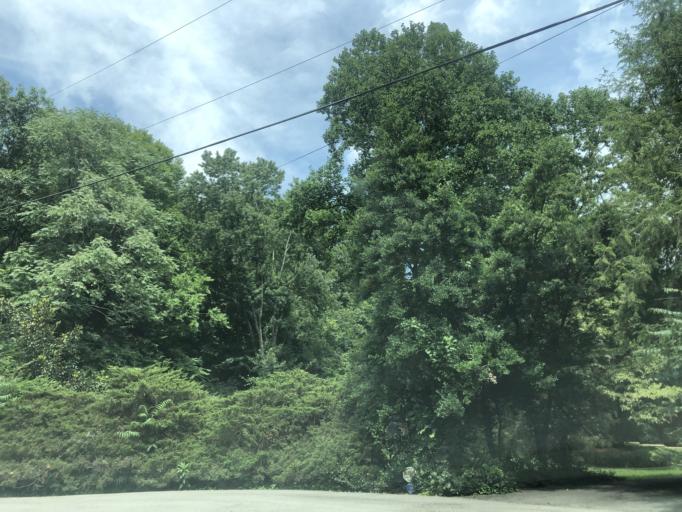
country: US
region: Tennessee
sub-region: Davidson County
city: Forest Hills
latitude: 36.0678
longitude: -86.8220
